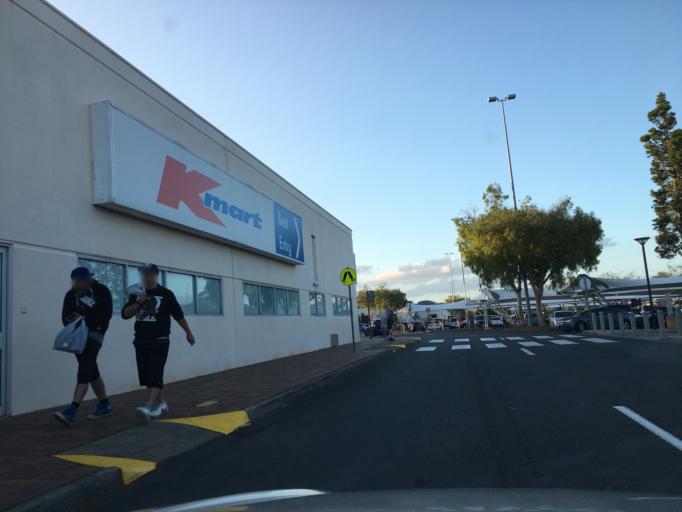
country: AU
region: Queensland
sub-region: Logan
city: Slacks Creek
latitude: -27.6605
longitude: 153.1733
